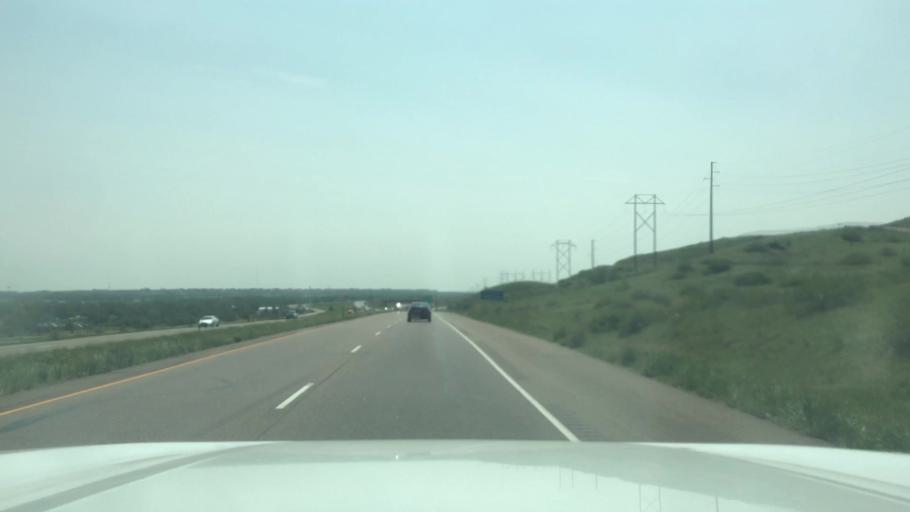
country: US
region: Colorado
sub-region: El Paso County
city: Security-Widefield
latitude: 38.7324
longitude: -104.7408
